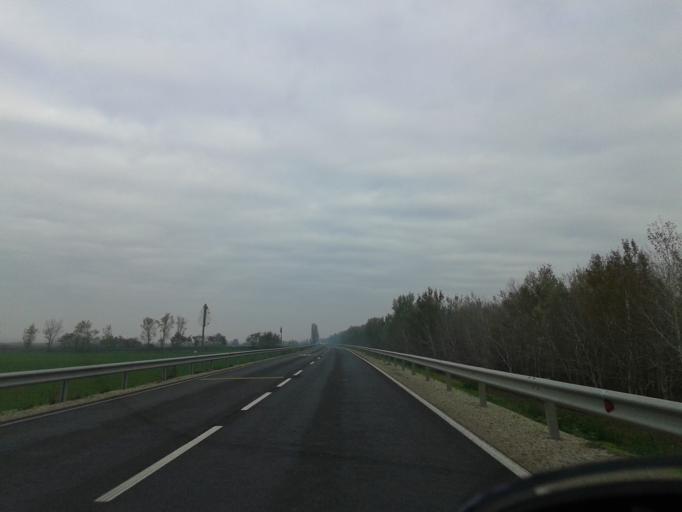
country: HU
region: Fejer
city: Ivancsa
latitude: 47.1820
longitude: 18.8691
